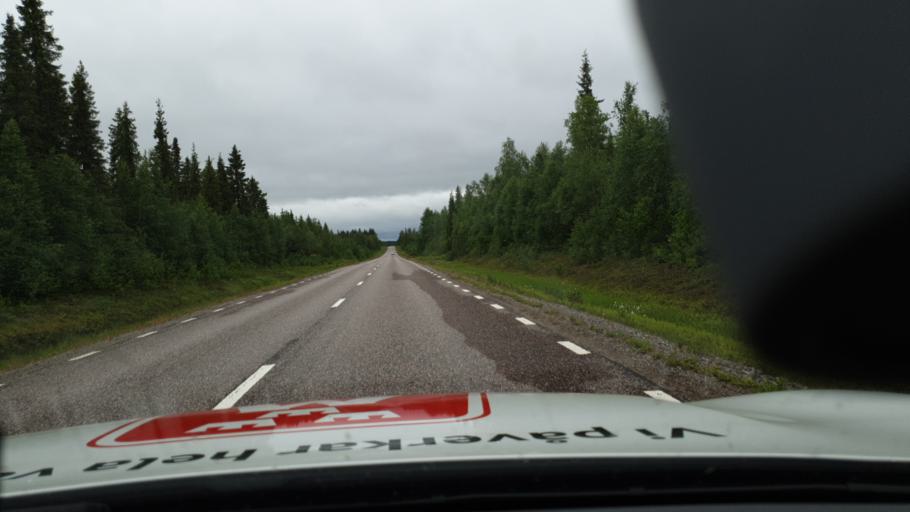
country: SE
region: Norrbotten
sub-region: Pajala Kommun
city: Pajala
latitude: 67.1414
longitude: 23.5732
